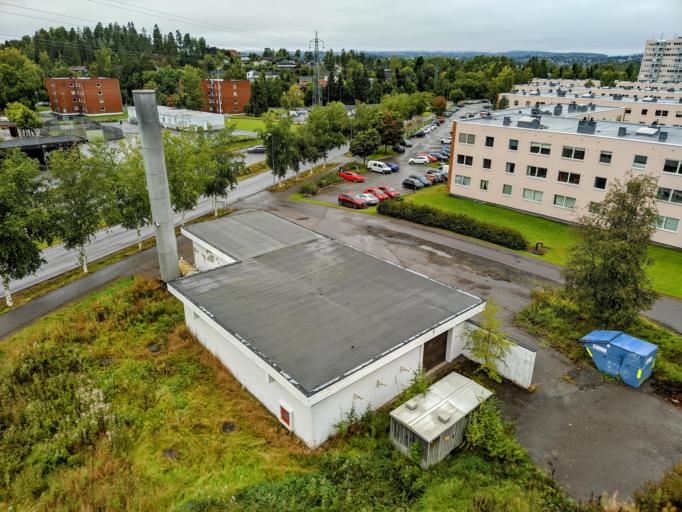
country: NO
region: Akershus
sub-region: Skedsmo
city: Lillestrom
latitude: 59.9374
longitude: 11.0276
